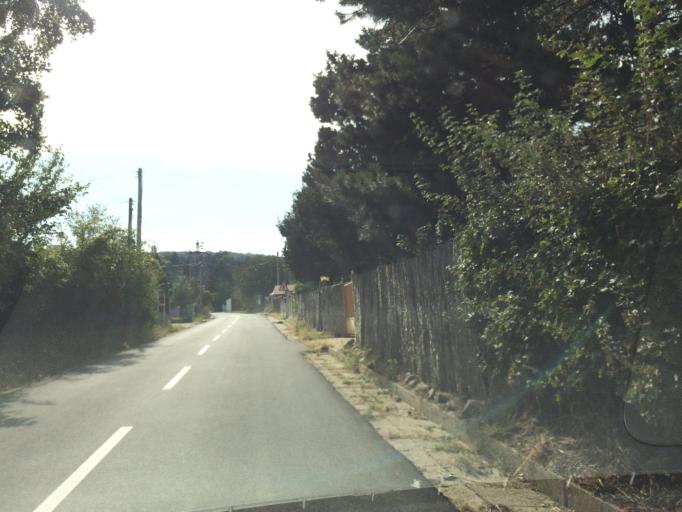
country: RS
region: Autonomna Pokrajina Vojvodina
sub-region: Juznobacki Okrug
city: Novi Sad
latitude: 45.1881
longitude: 19.8318
